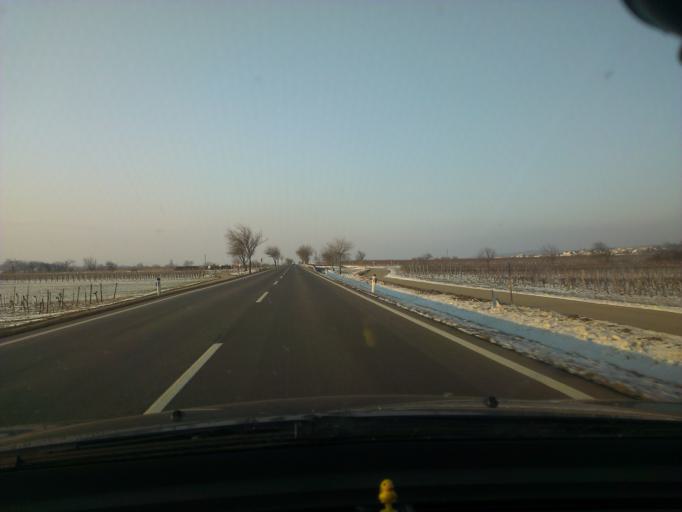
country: AT
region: Burgenland
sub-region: Eisenstadt-Umgebung
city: Breitenbrunn
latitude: 47.9271
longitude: 16.7128
